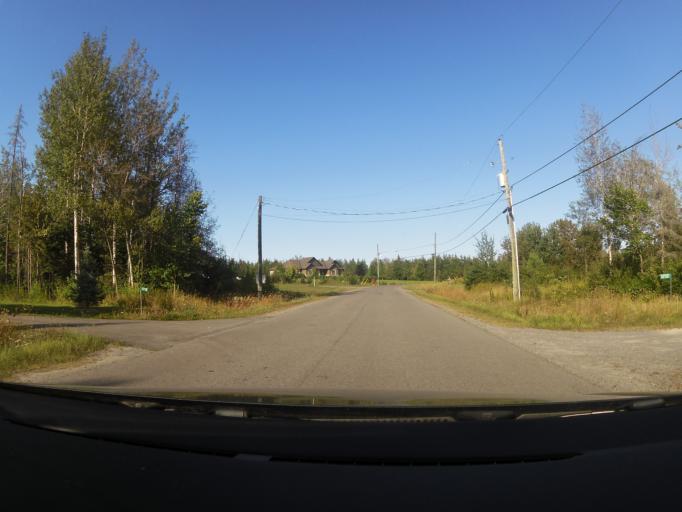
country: CA
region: Ontario
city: Carleton Place
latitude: 45.2884
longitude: -76.1106
